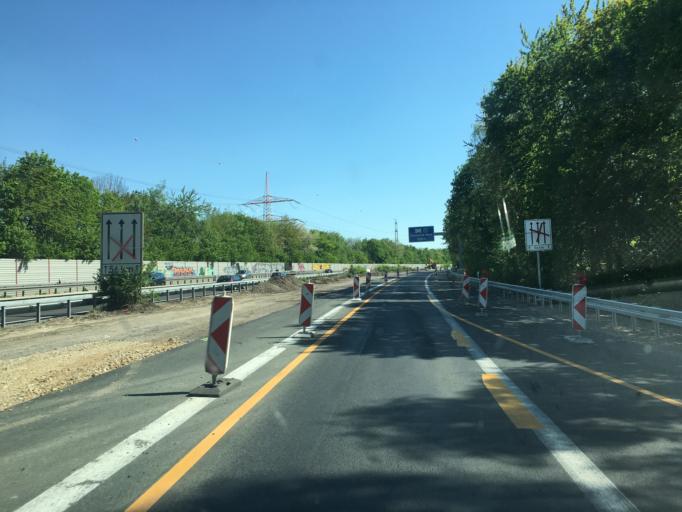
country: DE
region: North Rhine-Westphalia
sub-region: Regierungsbezirk Arnsberg
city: Dortmund
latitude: 51.5153
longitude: 7.3887
